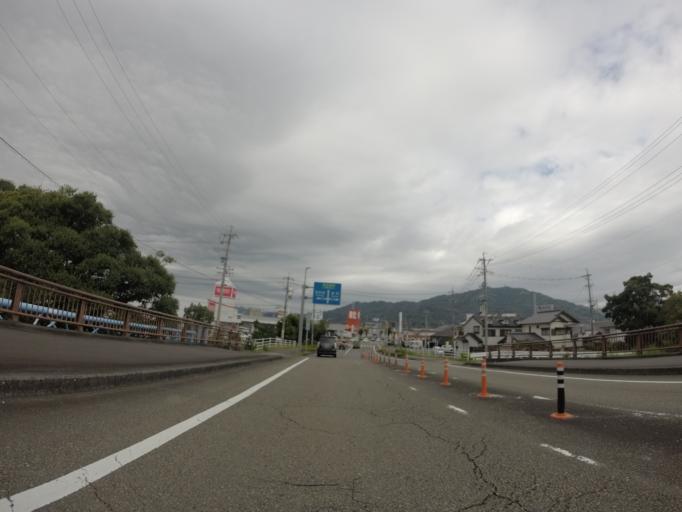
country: JP
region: Shizuoka
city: Yaizu
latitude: 34.8766
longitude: 138.3057
